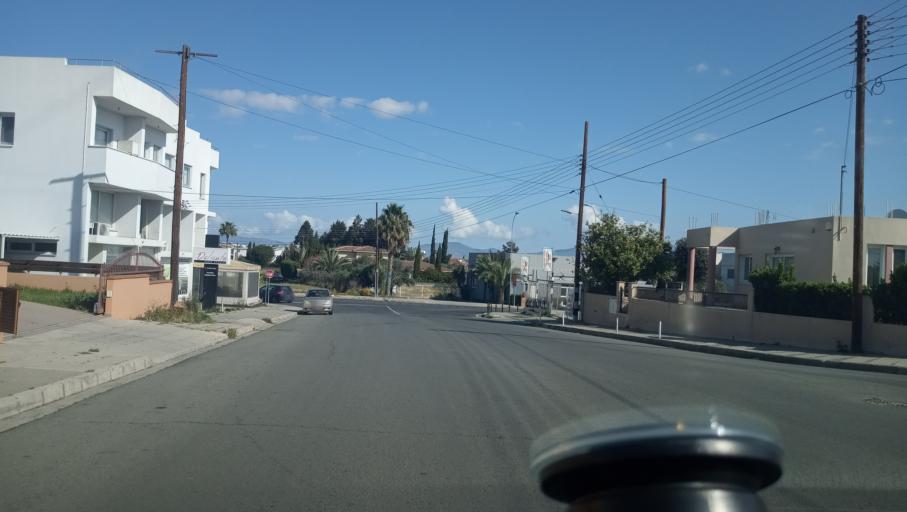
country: CY
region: Lefkosia
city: Geri
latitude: 35.1047
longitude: 33.3920
